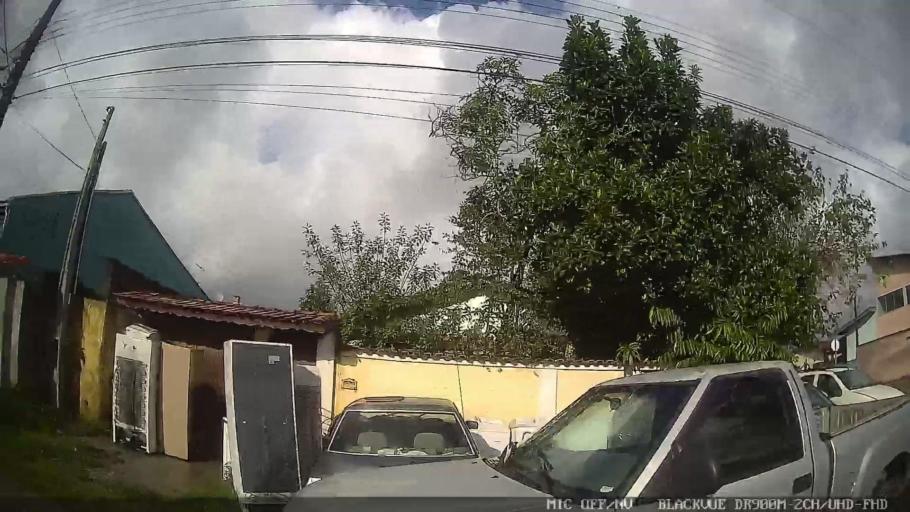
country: BR
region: Sao Paulo
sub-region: Itanhaem
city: Itanhaem
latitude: -24.2192
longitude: -46.8855
